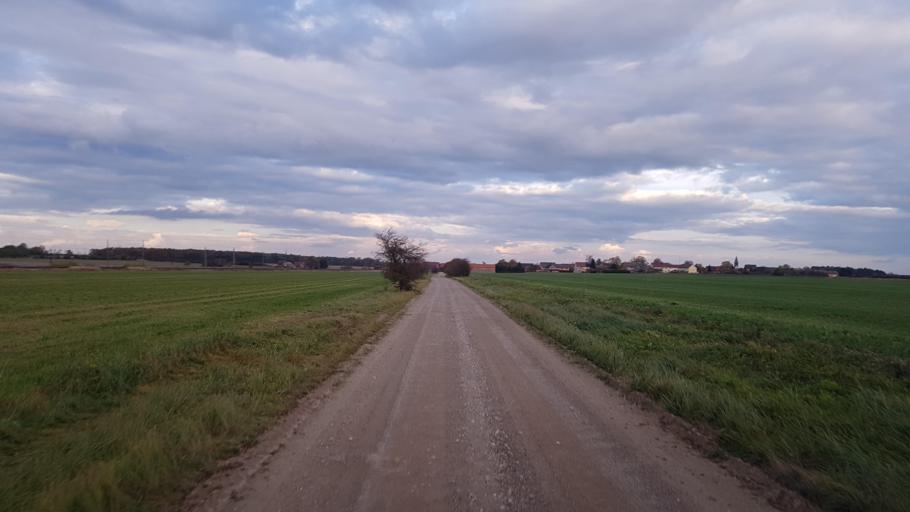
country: DE
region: Saxony-Anhalt
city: Zahna
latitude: 51.9473
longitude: 12.8559
